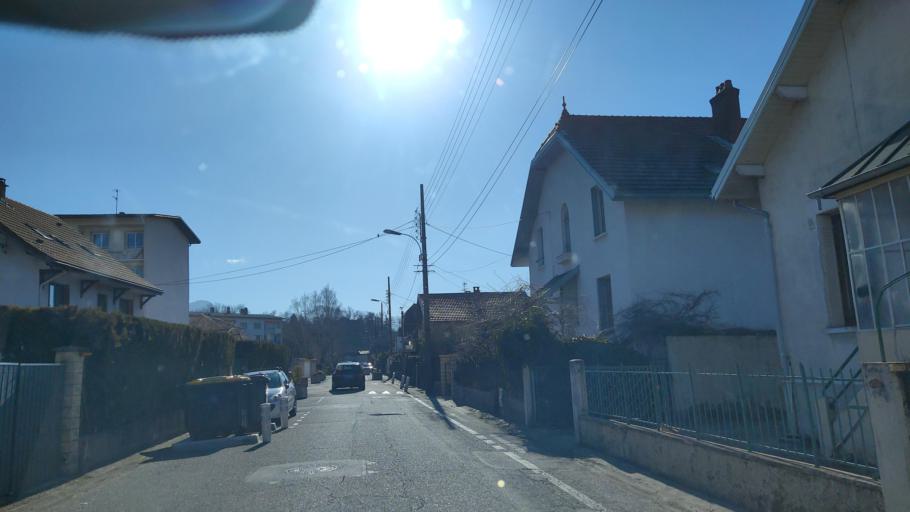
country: FR
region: Rhone-Alpes
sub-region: Departement de la Savoie
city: Chambery
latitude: 45.5672
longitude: 5.9466
